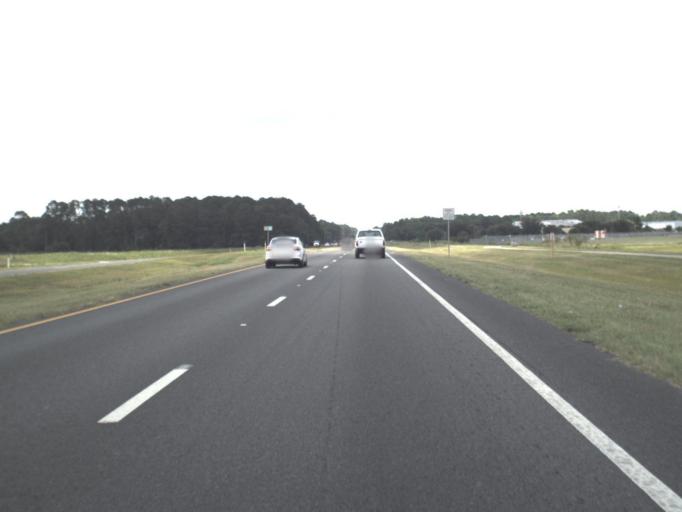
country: US
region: Florida
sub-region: Alachua County
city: Gainesville
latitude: 29.6893
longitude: -82.2862
